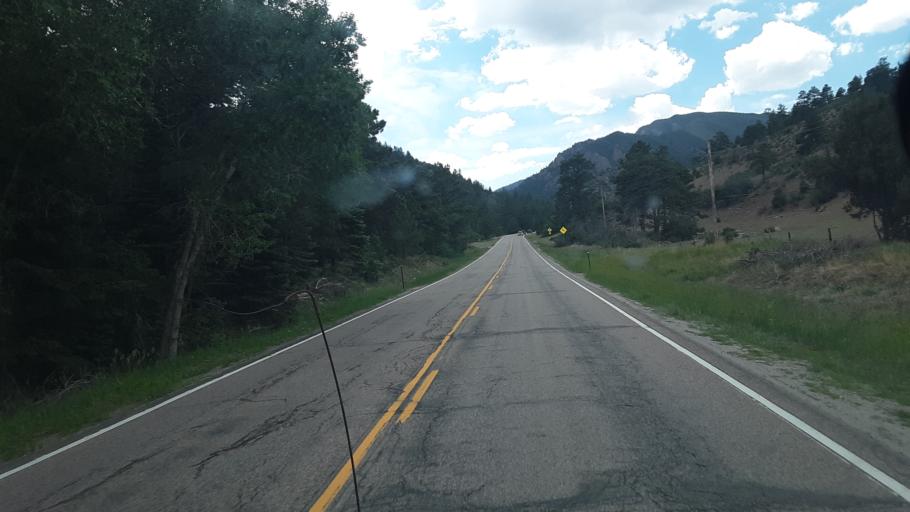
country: US
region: Colorado
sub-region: Fremont County
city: Florence
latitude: 38.1758
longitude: -105.1268
